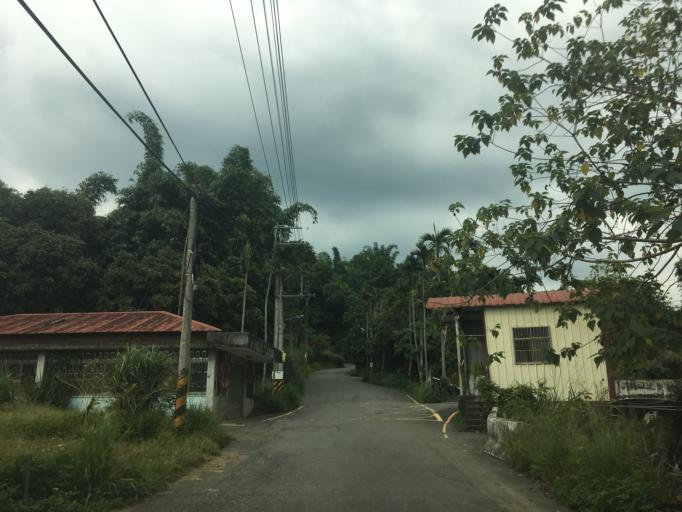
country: TW
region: Taiwan
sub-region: Taichung City
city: Taichung
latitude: 24.1688
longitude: 120.7588
